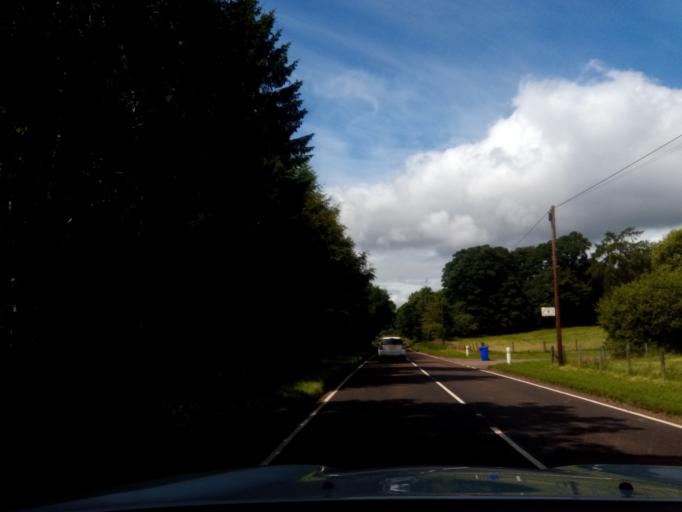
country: GB
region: Scotland
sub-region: Stirling
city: Doune
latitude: 56.2077
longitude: -4.1259
